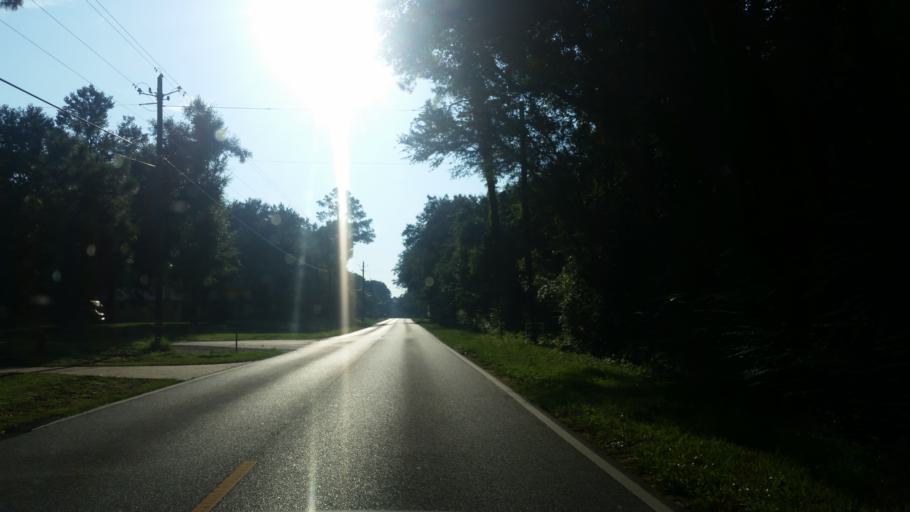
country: US
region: Florida
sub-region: Escambia County
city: Ensley
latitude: 30.5199
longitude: -87.3278
